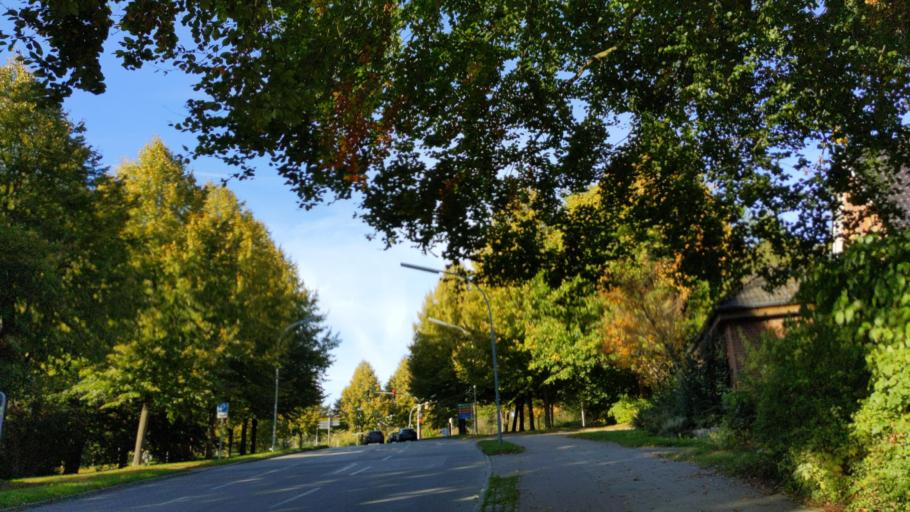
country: DE
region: Schleswig-Holstein
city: Eutin
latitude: 54.1490
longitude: 10.6075
